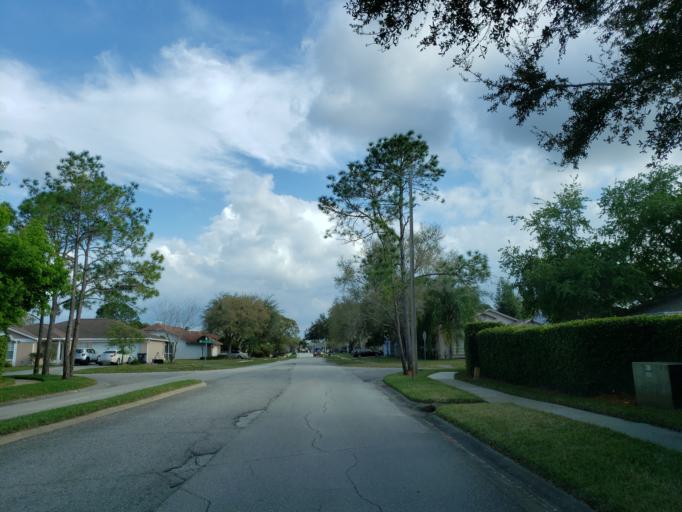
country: US
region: Florida
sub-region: Hillsborough County
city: Brandon
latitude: 27.9093
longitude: -82.3123
